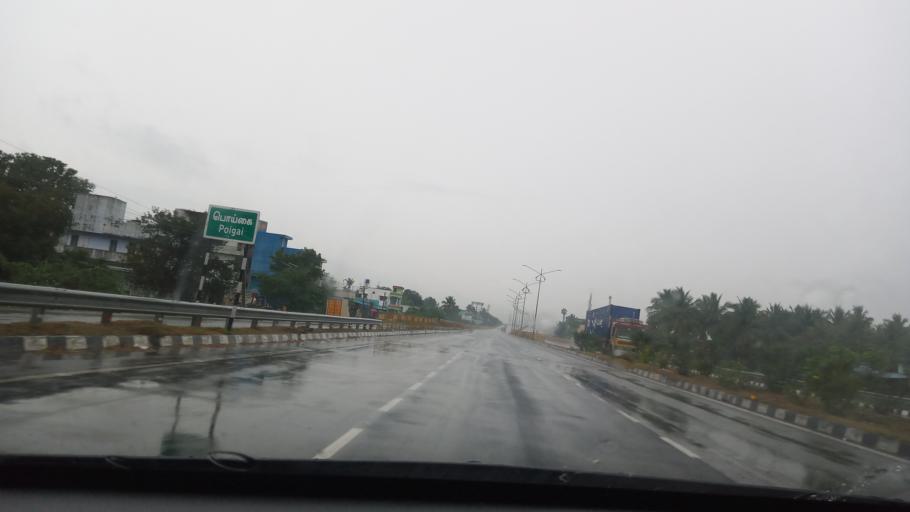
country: IN
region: Tamil Nadu
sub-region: Vellore
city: Vellore
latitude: 12.9158
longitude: 79.0553
